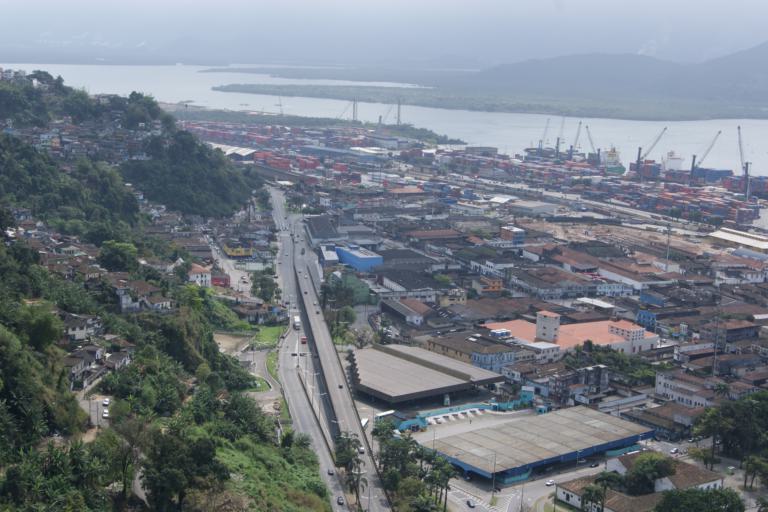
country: BR
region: Sao Paulo
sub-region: Santos
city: Santos
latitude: -23.9391
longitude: -46.3304
